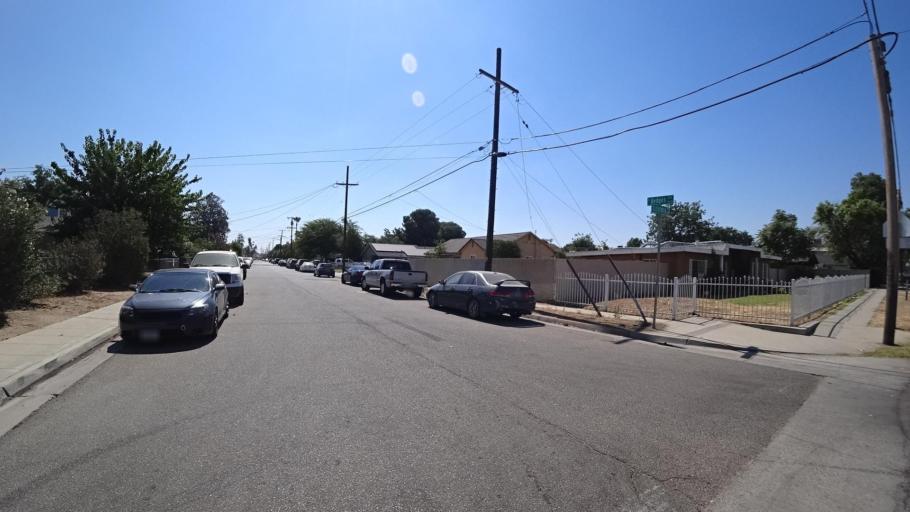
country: US
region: California
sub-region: Fresno County
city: Fresno
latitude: 36.7595
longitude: -119.7567
